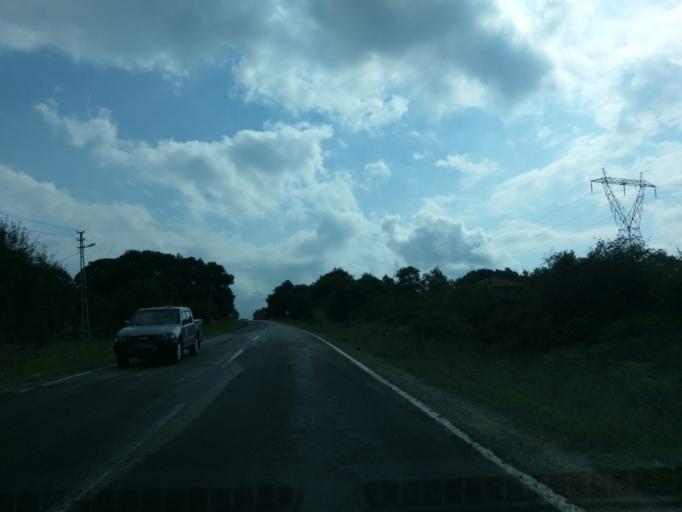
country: TR
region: Sinop
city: Erfelek
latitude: 41.9464
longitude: 34.7900
